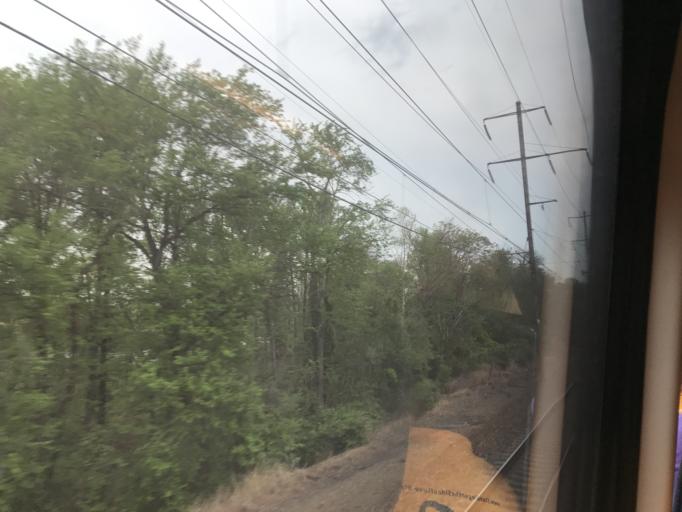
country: US
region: Maryland
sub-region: Prince George's County
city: Landover
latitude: 38.9315
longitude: -76.8946
